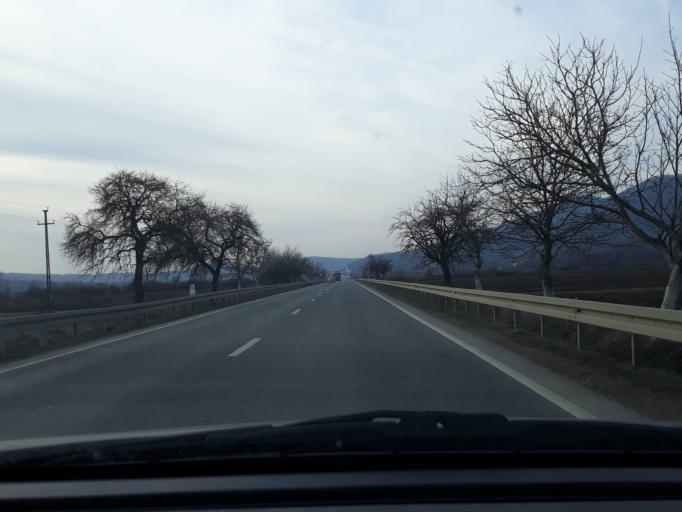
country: RO
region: Salaj
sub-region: Oras Simleu Silvaniei
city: Simleu Silvaniei
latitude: 47.2287
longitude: 22.8403
